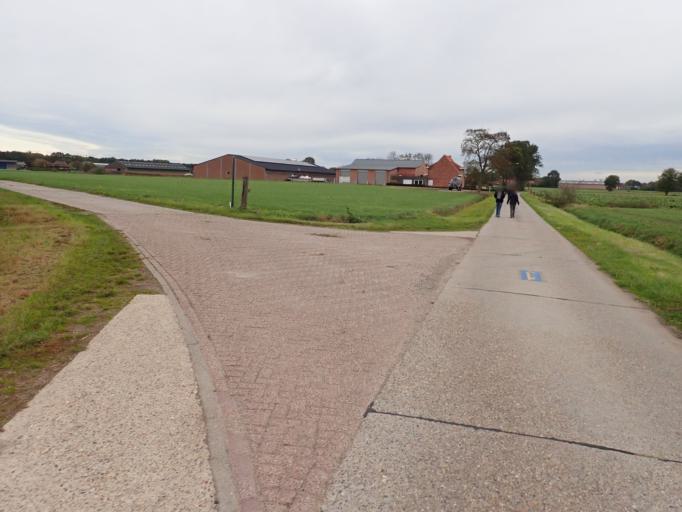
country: BE
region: Flanders
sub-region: Provincie Antwerpen
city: Wuustwezel
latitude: 51.3821
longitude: 4.5752
